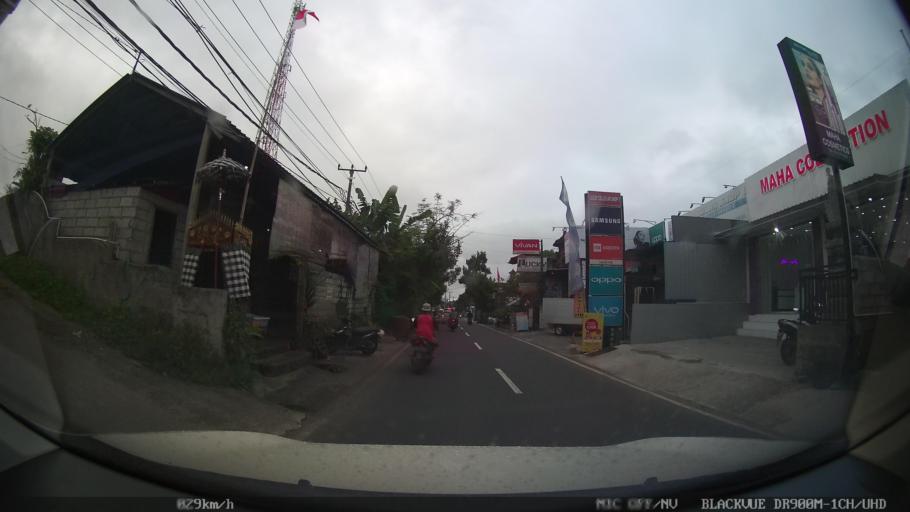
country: ID
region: Bali
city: Badung
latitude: -8.4204
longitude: 115.2452
